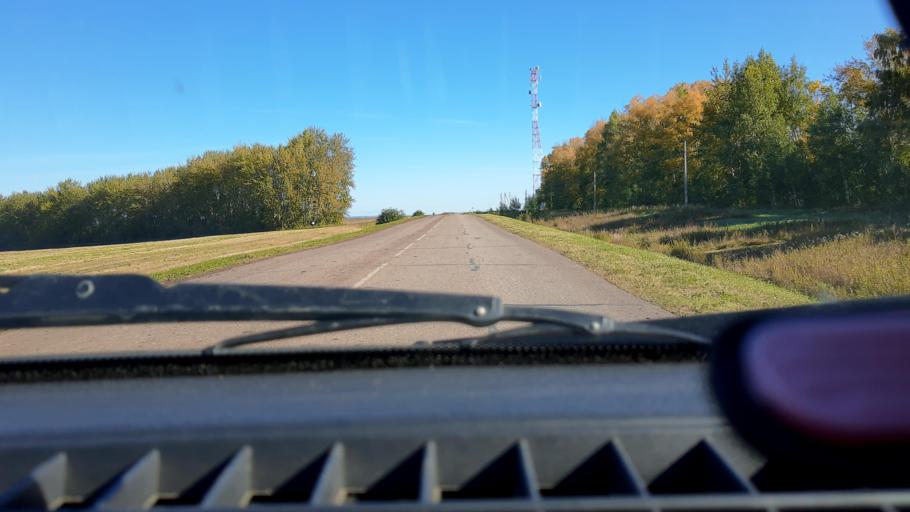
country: RU
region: Bashkortostan
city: Kushnarenkovo
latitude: 55.0713
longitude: 55.4552
